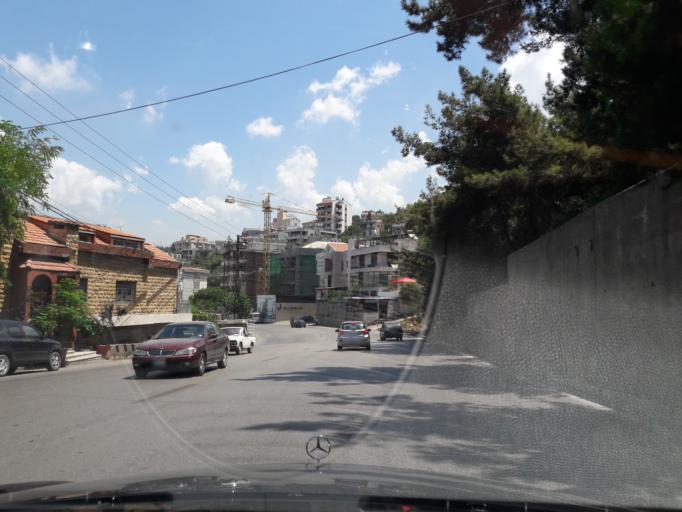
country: LB
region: Mont-Liban
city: Djounie
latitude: 33.9235
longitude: 35.6329
